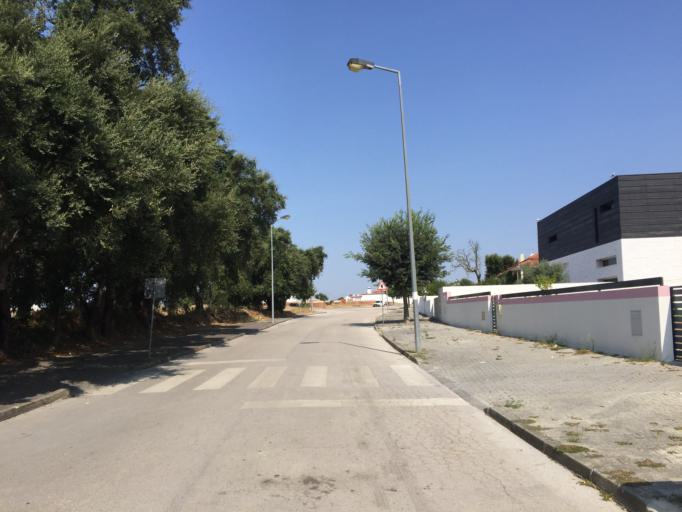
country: PT
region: Setubal
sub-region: Setubal
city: Setubal
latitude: 38.5865
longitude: -8.6896
